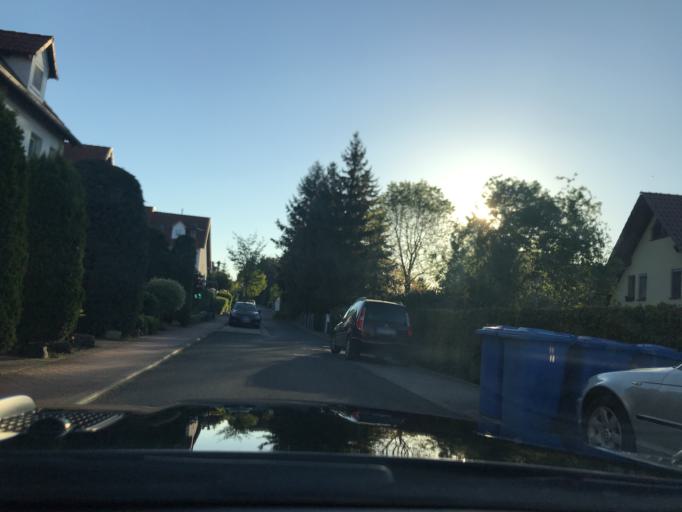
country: DE
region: Thuringia
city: Muehlhausen
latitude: 51.2001
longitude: 10.4386
